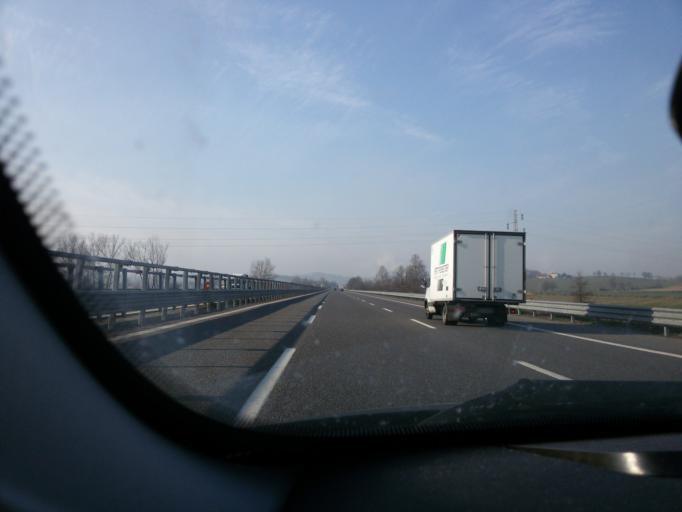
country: IT
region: Piedmont
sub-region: Provincia di Alessandria
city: Castelletto Monferrato
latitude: 44.9599
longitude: 8.5568
